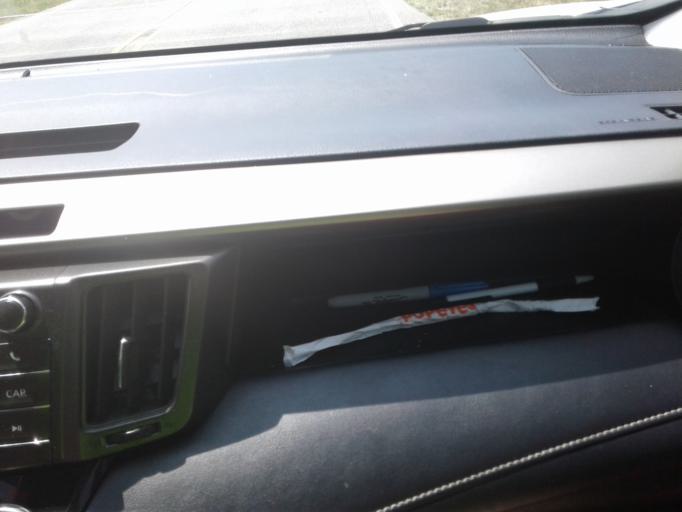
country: US
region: North Carolina
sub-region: Harnett County
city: Coats
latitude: 35.4512
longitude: -78.6867
